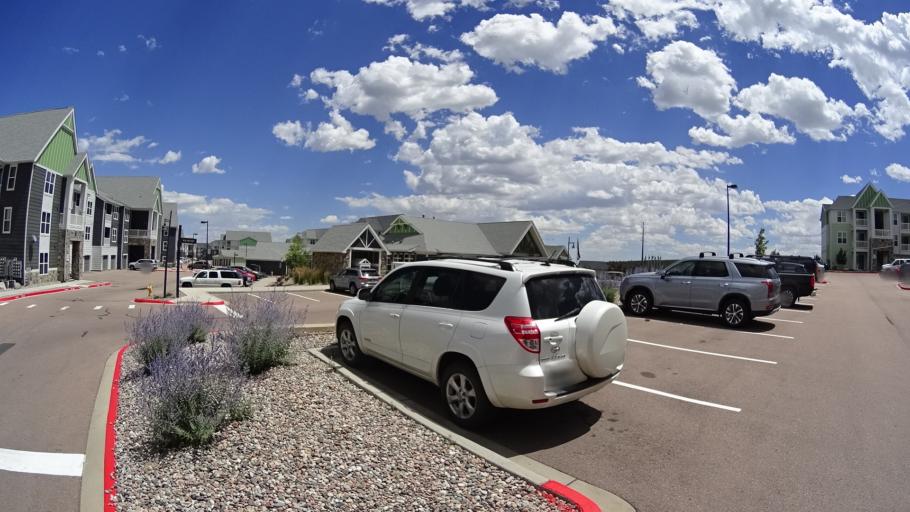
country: US
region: Colorado
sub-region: El Paso County
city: Black Forest
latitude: 38.9437
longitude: -104.7116
